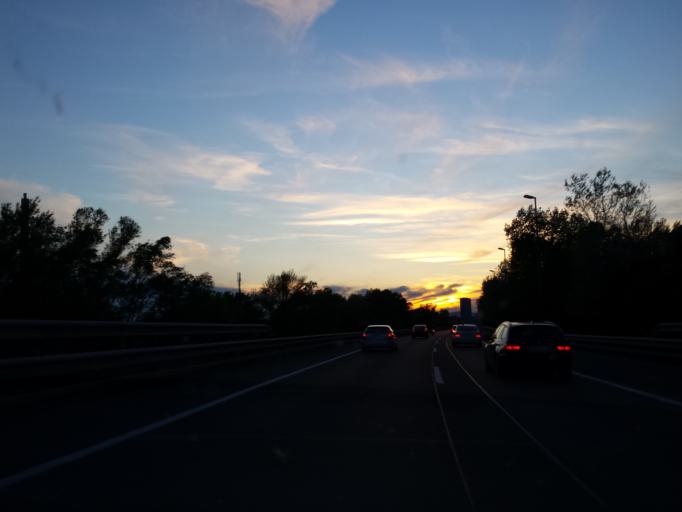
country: AT
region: Lower Austria
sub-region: Politischer Bezirk Wien-Umgebung
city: Schwechat
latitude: 48.1846
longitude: 16.4398
